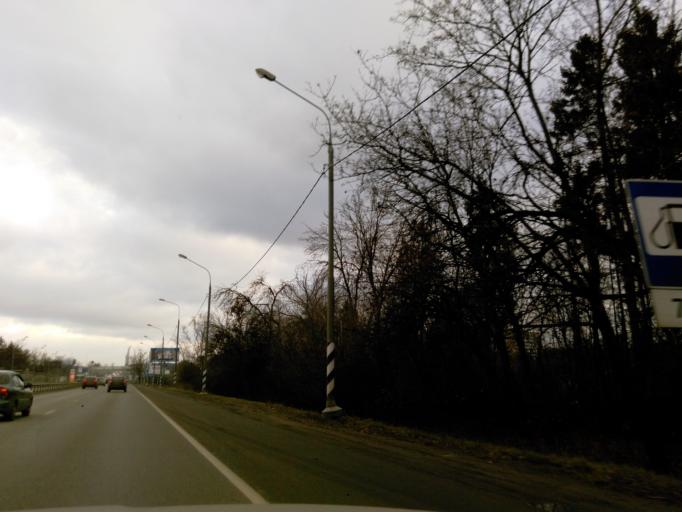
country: RU
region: Moskovskaya
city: Rzhavki
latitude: 56.0052
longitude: 37.2308
